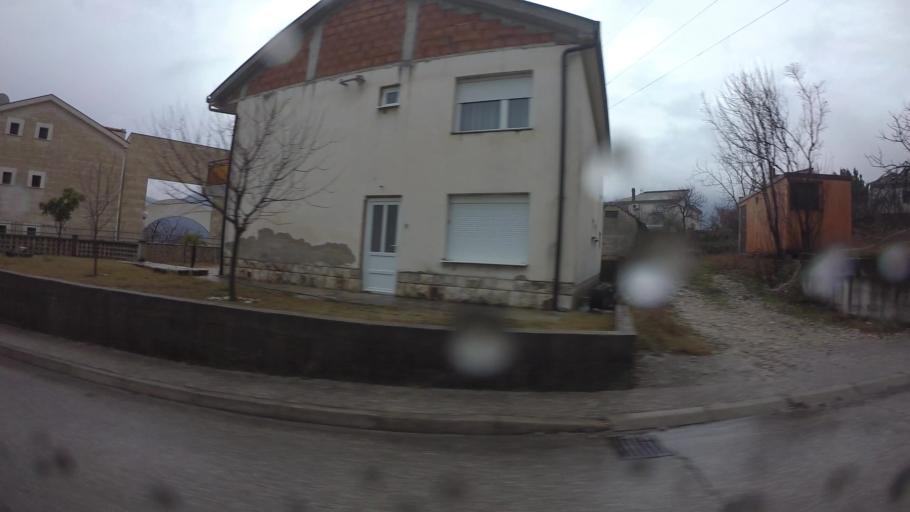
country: BA
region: Federation of Bosnia and Herzegovina
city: Cim
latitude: 43.3545
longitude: 17.7757
